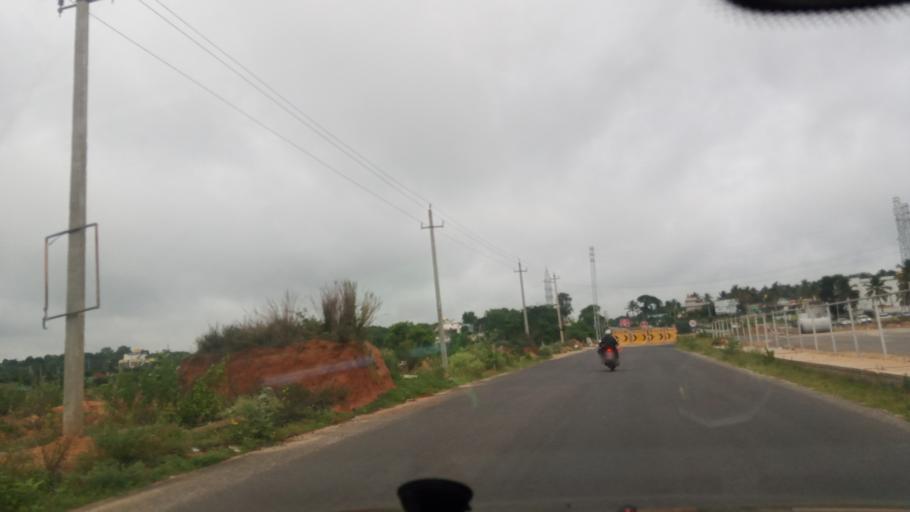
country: IN
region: Karnataka
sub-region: Ramanagara
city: Ramanagaram
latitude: 12.7690
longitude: 77.3397
